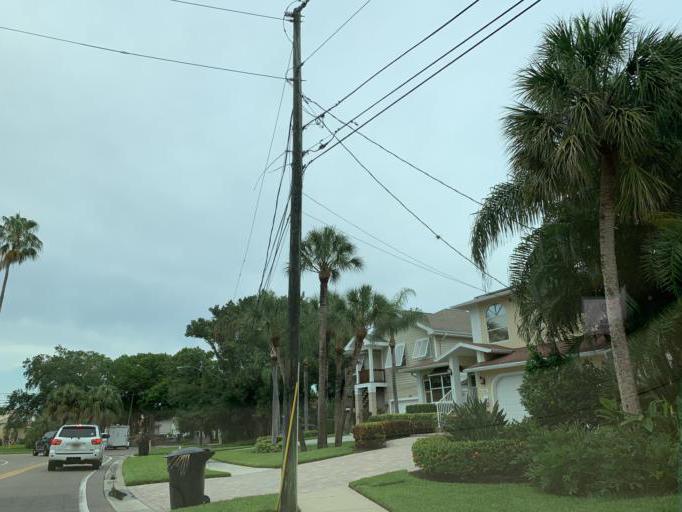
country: US
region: Florida
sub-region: Pinellas County
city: Gandy
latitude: 27.8214
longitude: -82.6068
